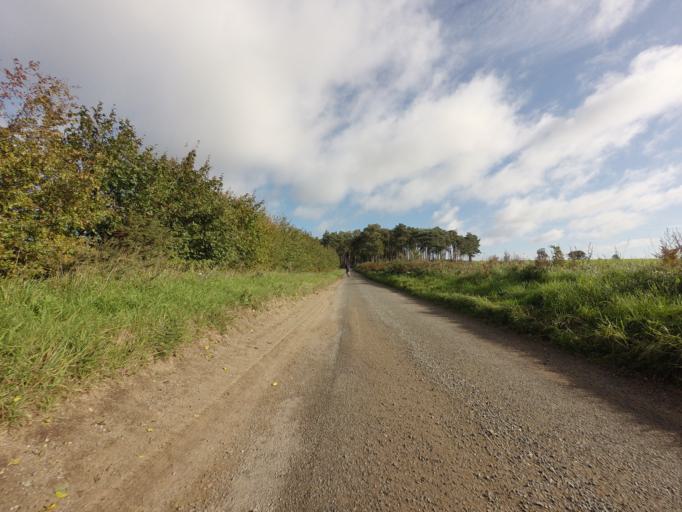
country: GB
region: England
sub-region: Norfolk
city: Dersingham
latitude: 52.8730
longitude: 0.6741
